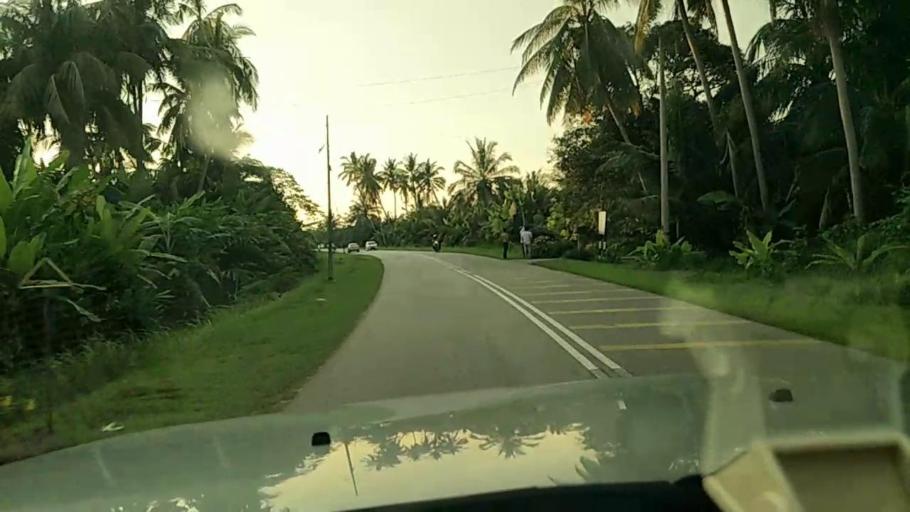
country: MY
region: Selangor
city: Kuala Selangor
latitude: 3.3049
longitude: 101.2953
